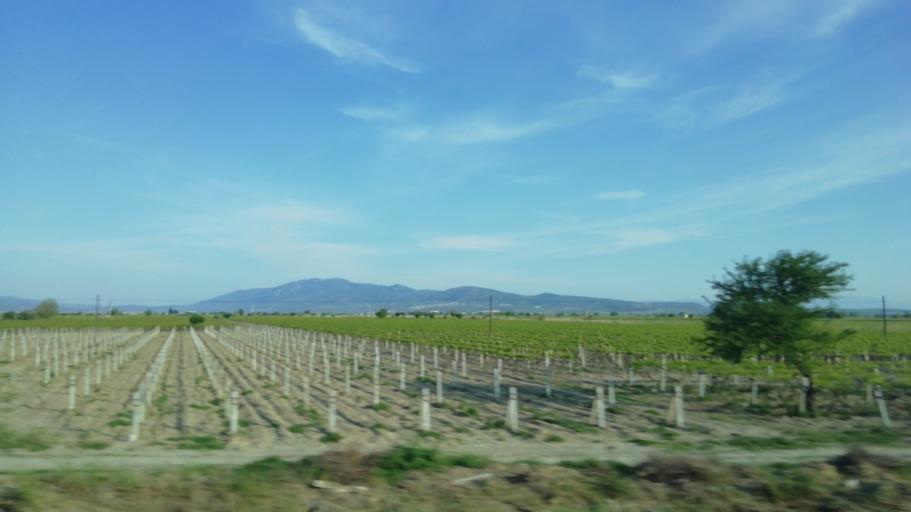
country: TR
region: Manisa
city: Saruhanli
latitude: 38.7511
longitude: 27.6237
